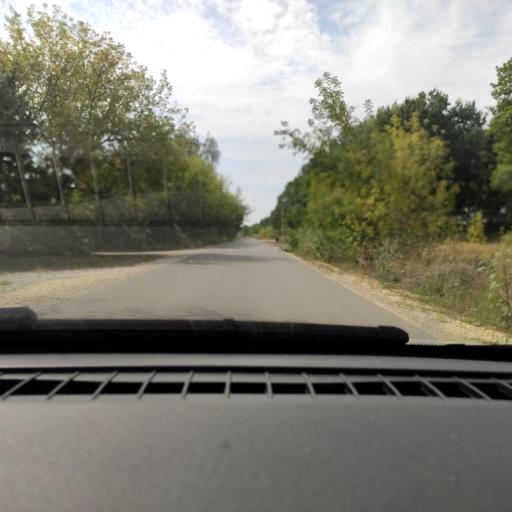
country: RU
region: Voronezj
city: Pridonskoy
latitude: 51.7381
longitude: 39.0665
